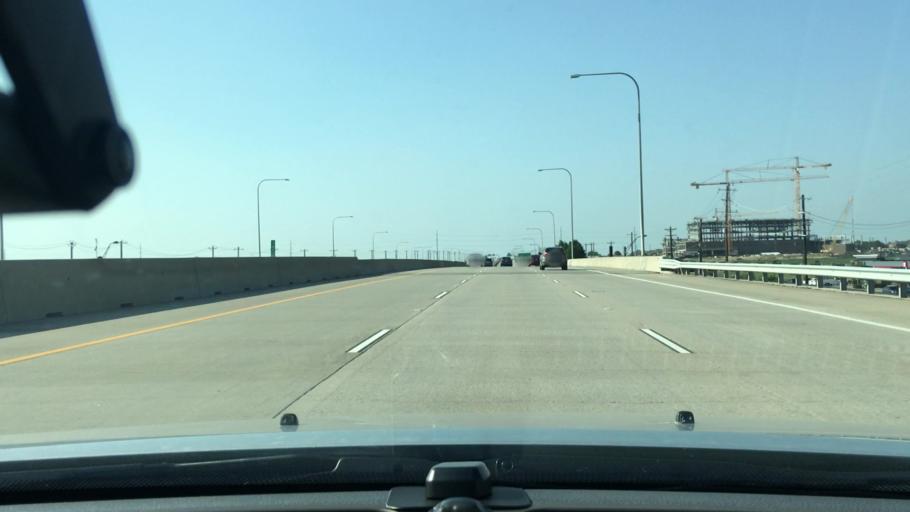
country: US
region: Texas
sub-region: Collin County
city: Frisco
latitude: 33.1741
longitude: -96.8395
